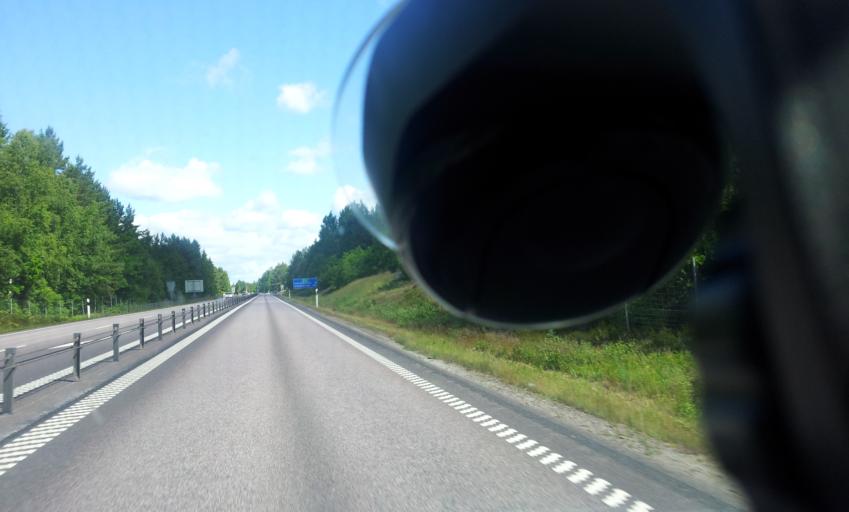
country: SE
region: Kalmar
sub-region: Oskarshamns Kommun
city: Paskallavik
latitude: 57.1994
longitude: 16.4376
